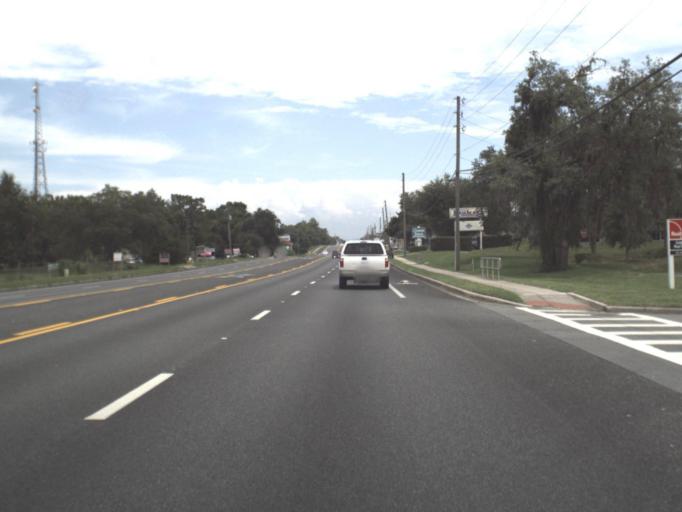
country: US
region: Florida
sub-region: Citrus County
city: Inverness Highlands North
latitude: 28.8490
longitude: -82.3743
